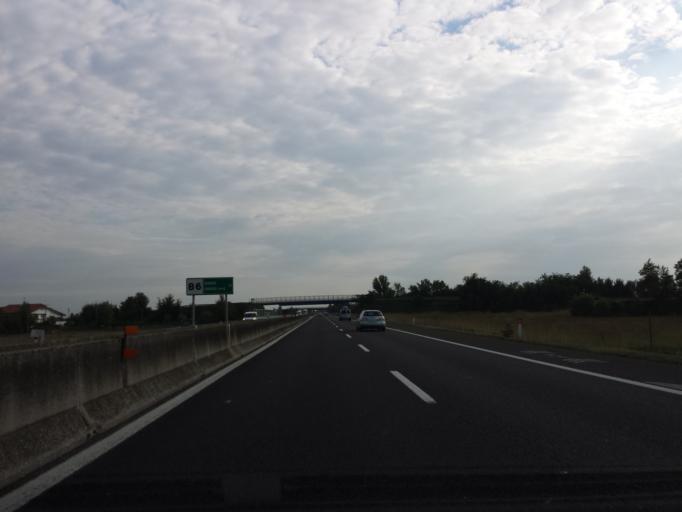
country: IT
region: Veneto
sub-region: Provincia di Padova
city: Pozzonovo
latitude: 45.2167
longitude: 11.7746
